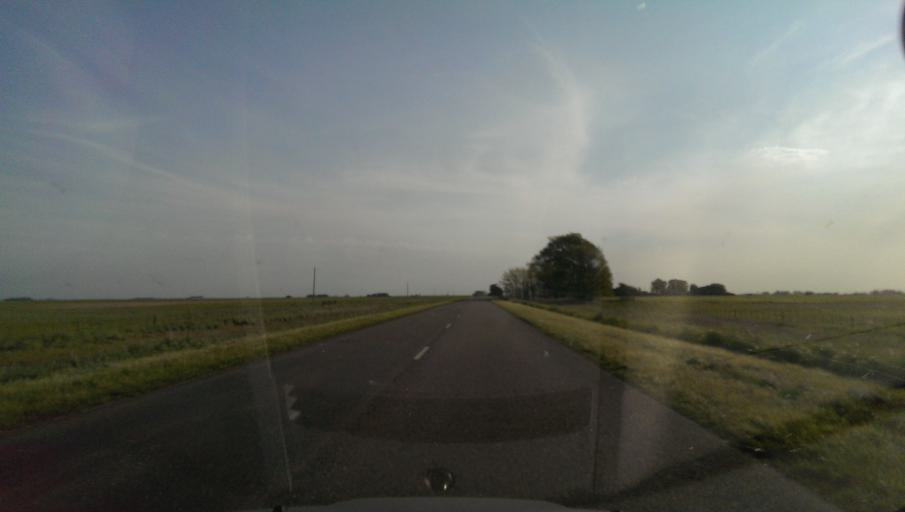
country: AR
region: Buenos Aires
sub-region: Partido de General La Madrid
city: General La Madrid
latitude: -37.5405
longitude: -61.2573
